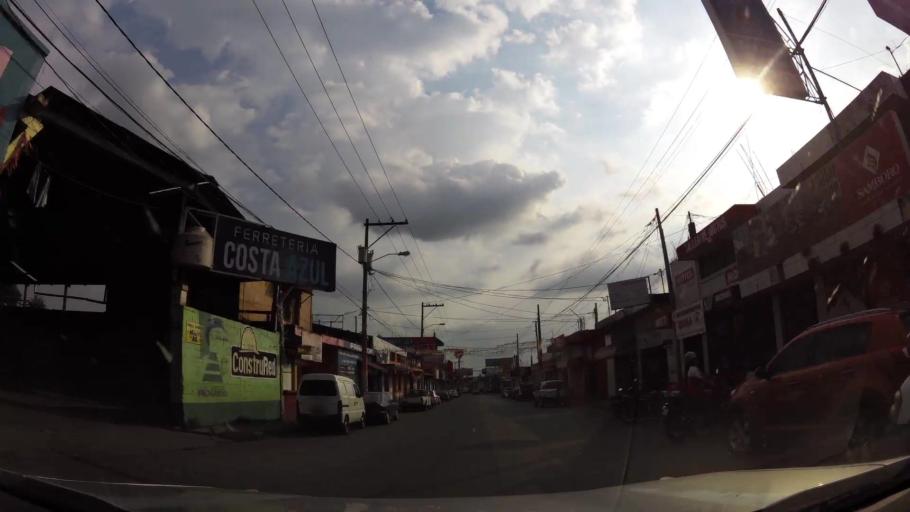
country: GT
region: Escuintla
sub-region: Municipio de Escuintla
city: Escuintla
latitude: 14.3070
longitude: -90.7840
